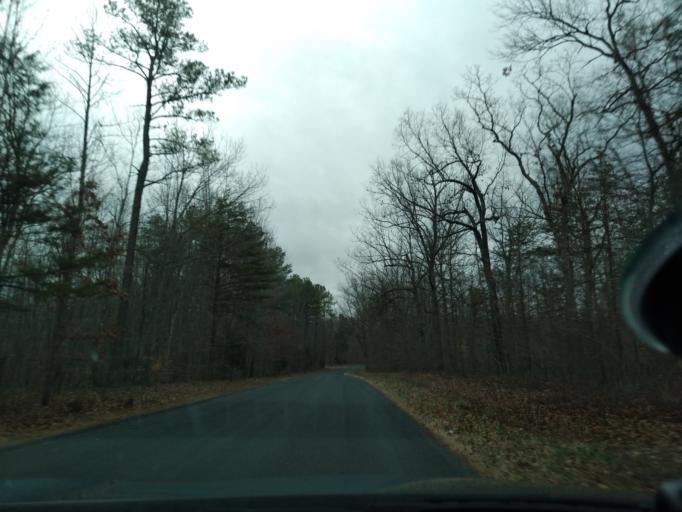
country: US
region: Virginia
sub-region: Appomattox County
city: Appomattox
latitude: 37.4051
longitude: -78.6664
